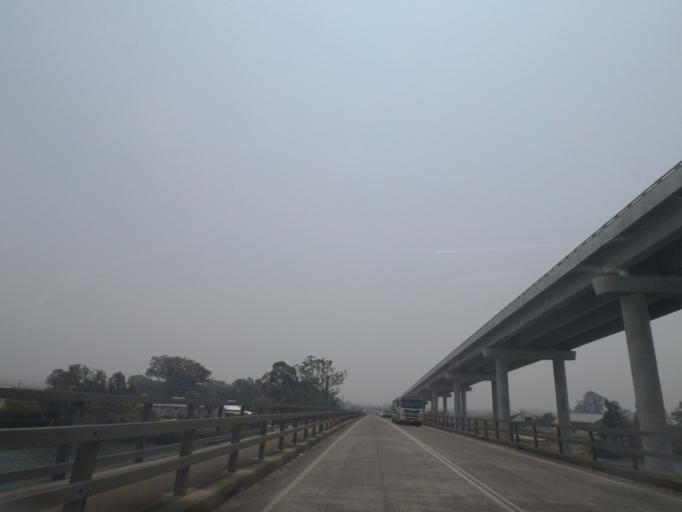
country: AU
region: New South Wales
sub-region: Clarence Valley
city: Maclean
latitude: -29.4294
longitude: 153.2407
